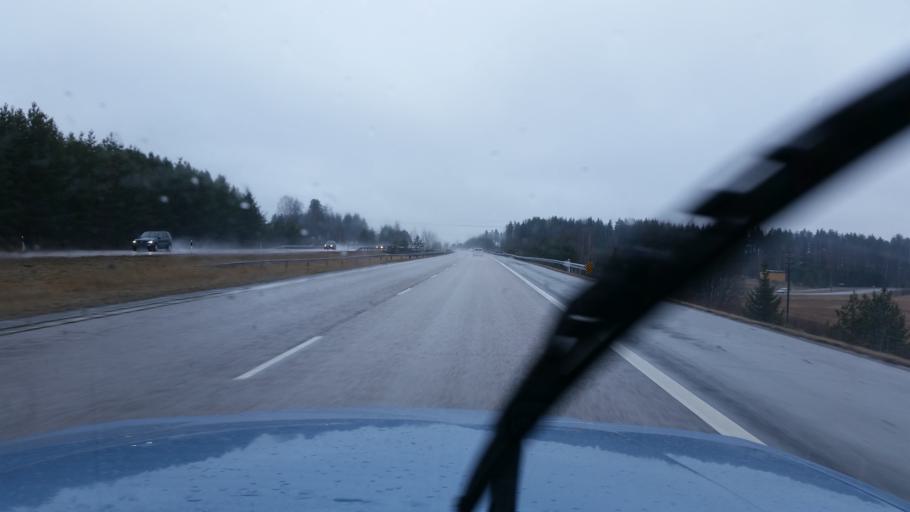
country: FI
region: Uusimaa
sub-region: Helsinki
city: Nurmijaervi
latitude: 60.4863
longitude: 24.8506
